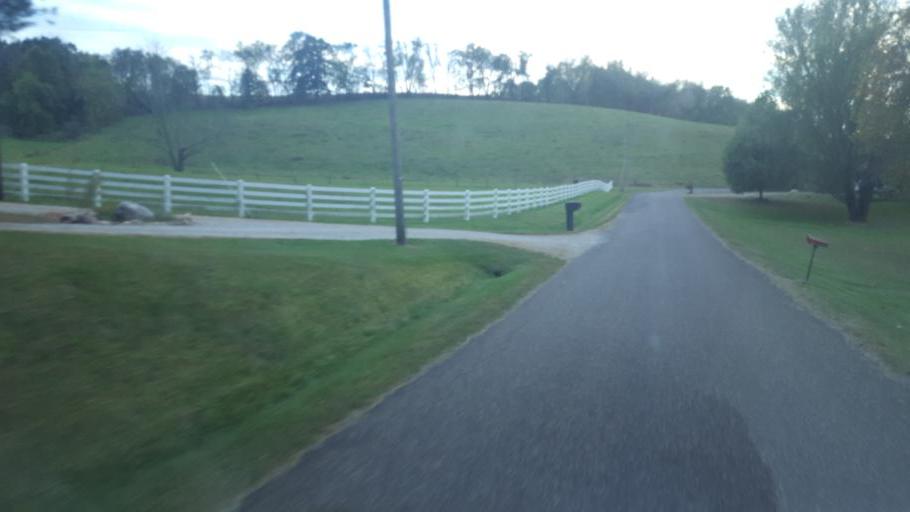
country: US
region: Ohio
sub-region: Ashland County
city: Loudonville
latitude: 40.6979
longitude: -82.2368
